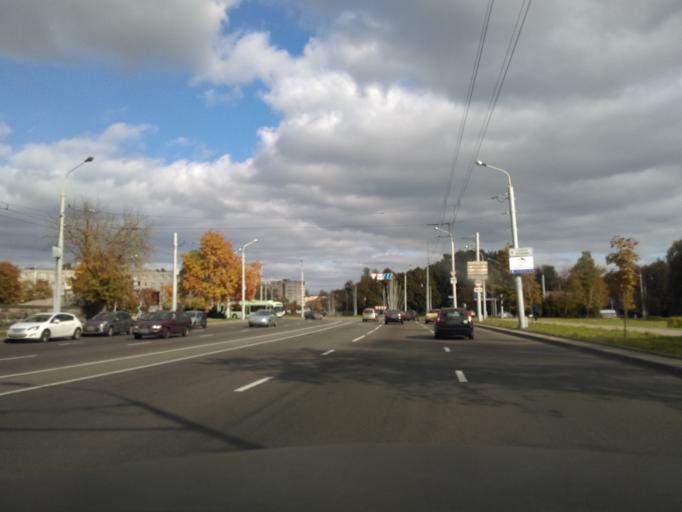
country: BY
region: Minsk
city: Minsk
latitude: 53.8778
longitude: 27.6086
